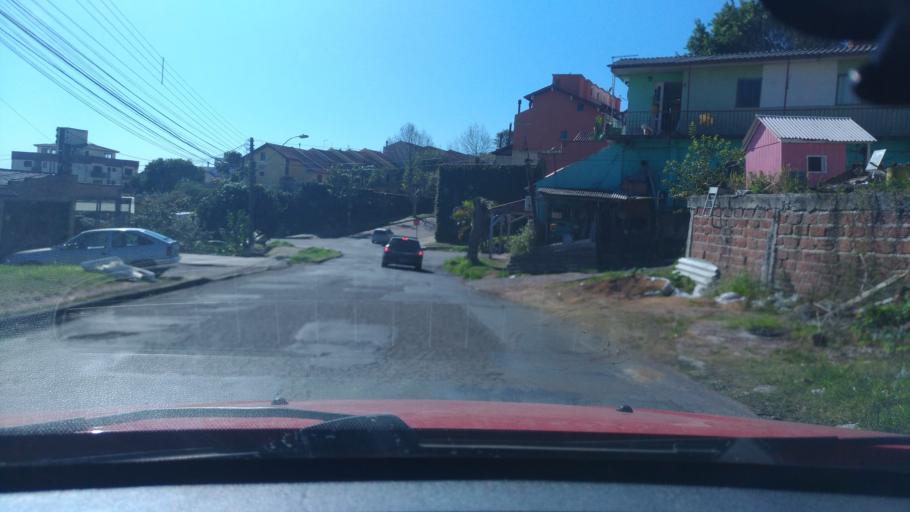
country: BR
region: Rio Grande do Sul
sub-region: Porto Alegre
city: Porto Alegre
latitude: -30.0344
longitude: -51.1488
